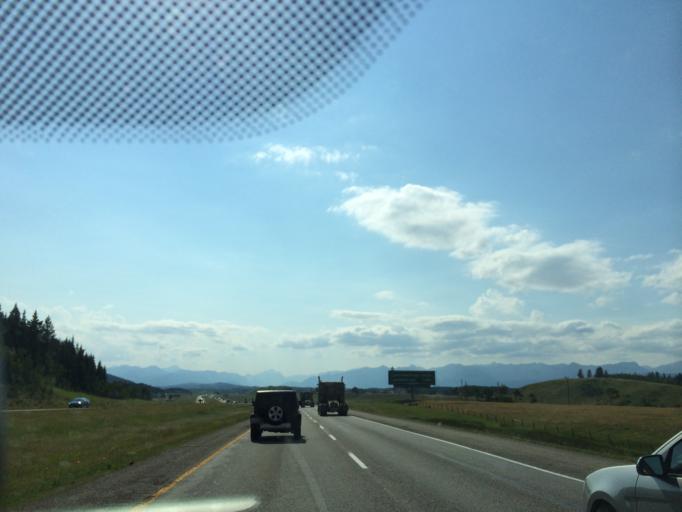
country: CA
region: Alberta
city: Cochrane
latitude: 51.1592
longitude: -114.7882
